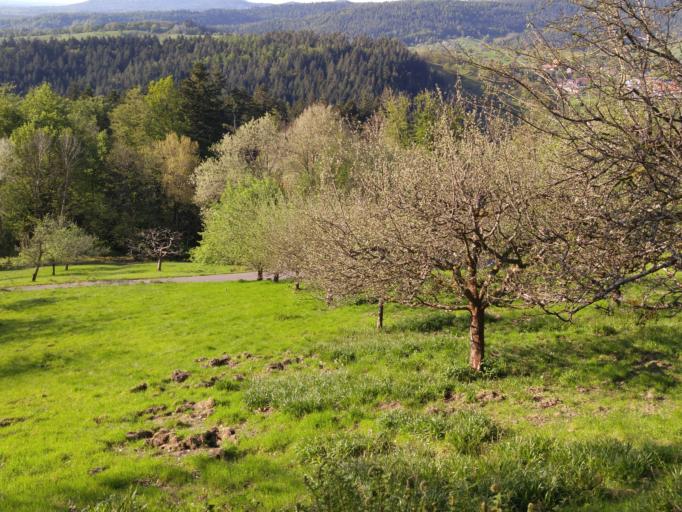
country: DE
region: Baden-Wuerttemberg
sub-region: Karlsruhe Region
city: Loffenau
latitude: 48.7611
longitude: 8.3765
